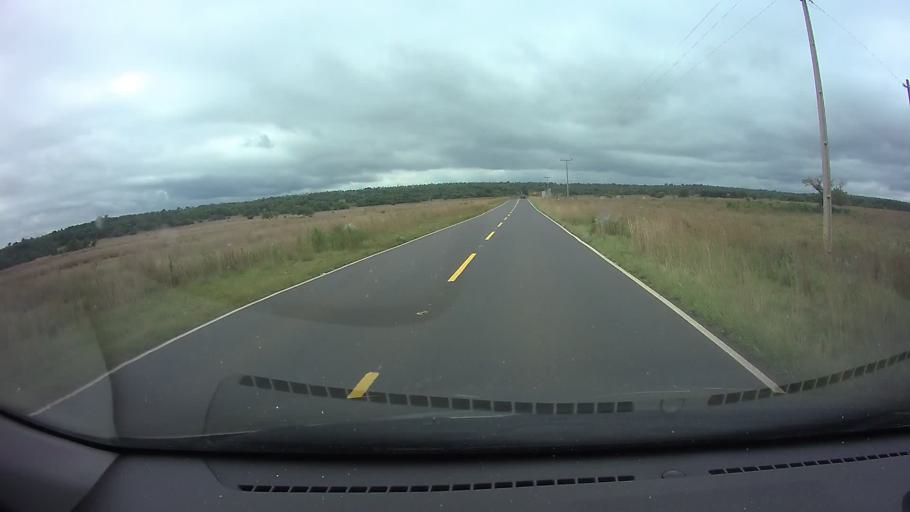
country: PY
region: Paraguari
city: Yaguaron
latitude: -25.7114
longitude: -57.3430
